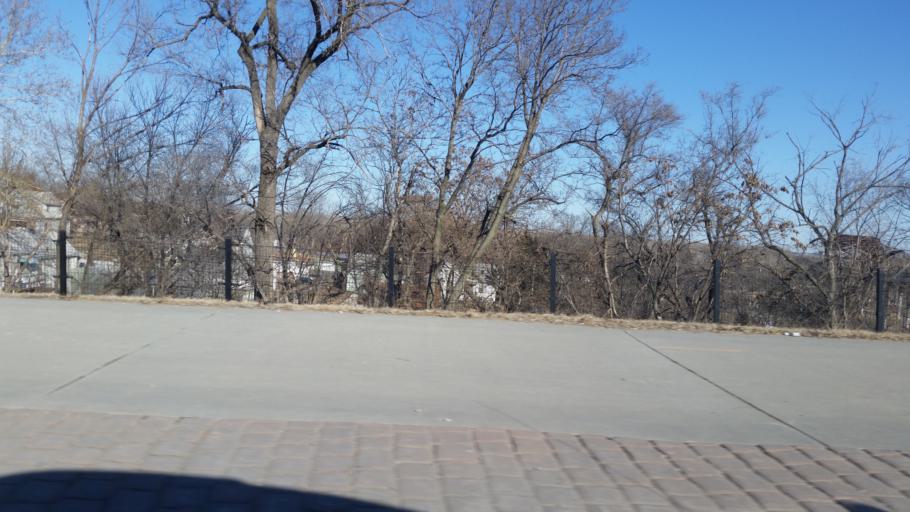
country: US
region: Nebraska
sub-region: Douglas County
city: Omaha
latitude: 41.2140
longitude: -95.9332
